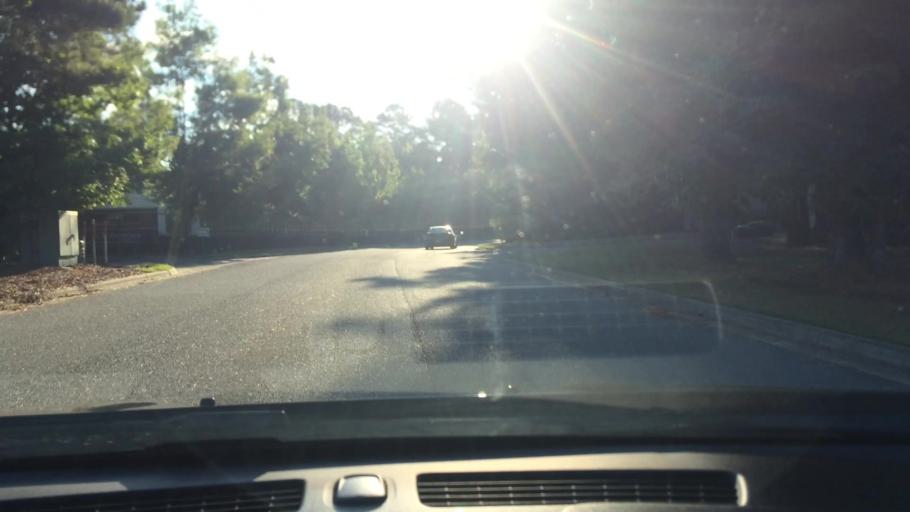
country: US
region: North Carolina
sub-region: Pitt County
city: Summerfield
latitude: 35.6031
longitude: -77.4050
